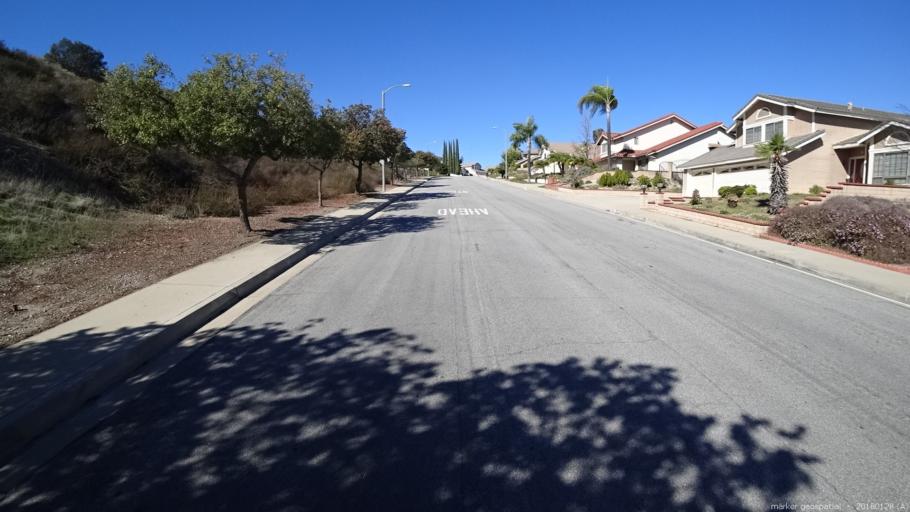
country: US
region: California
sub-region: Los Angeles County
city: Diamond Bar
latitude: 34.0044
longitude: -117.7912
